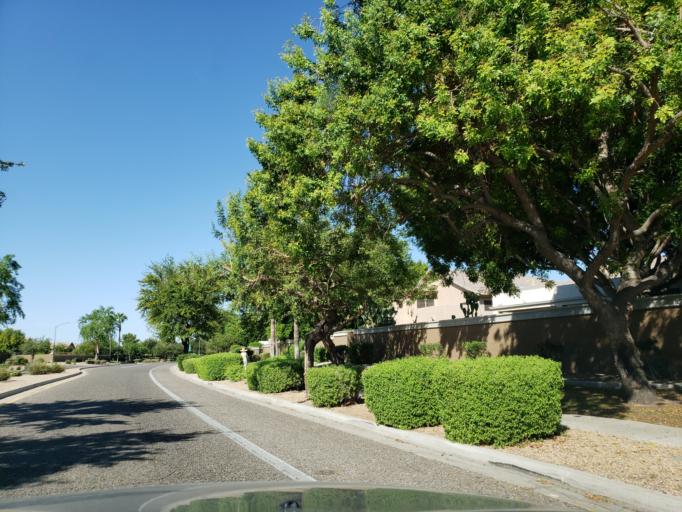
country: US
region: Arizona
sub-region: Maricopa County
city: Peoria
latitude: 33.6610
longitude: -112.1973
